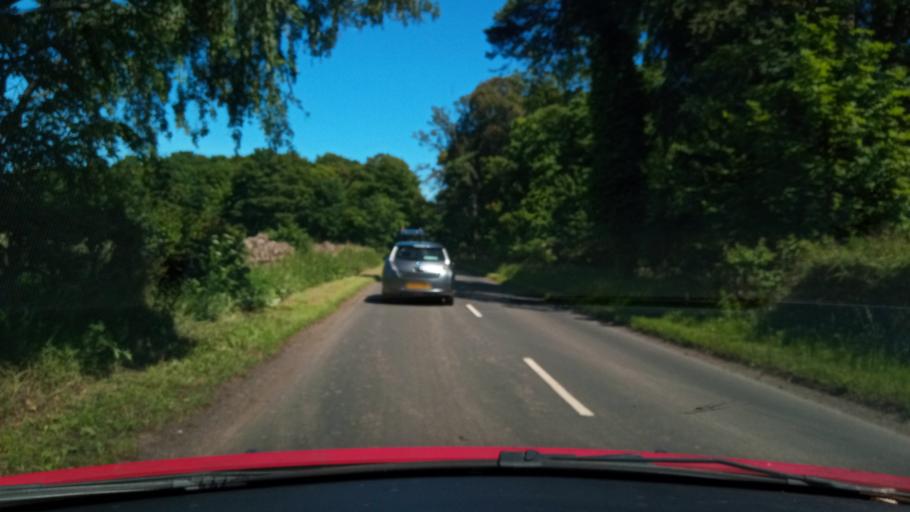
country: GB
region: Scotland
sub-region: East Lothian
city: Gullane
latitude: 56.0085
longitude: -2.8421
